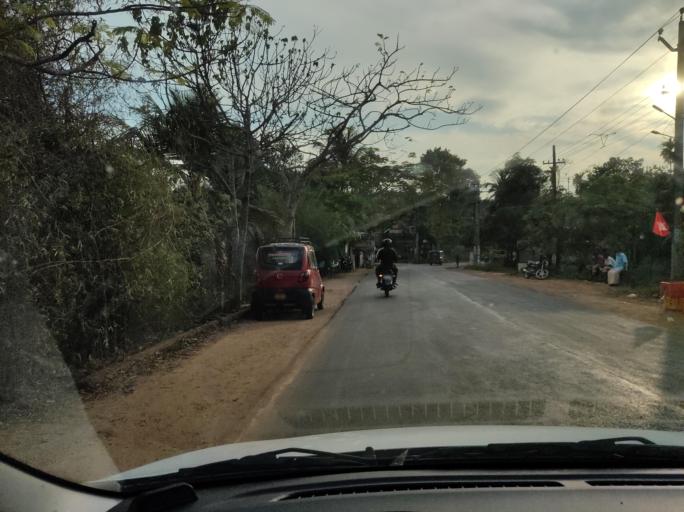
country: IN
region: Kerala
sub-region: Kottayam
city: Vaikam
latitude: 9.6931
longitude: 76.4750
